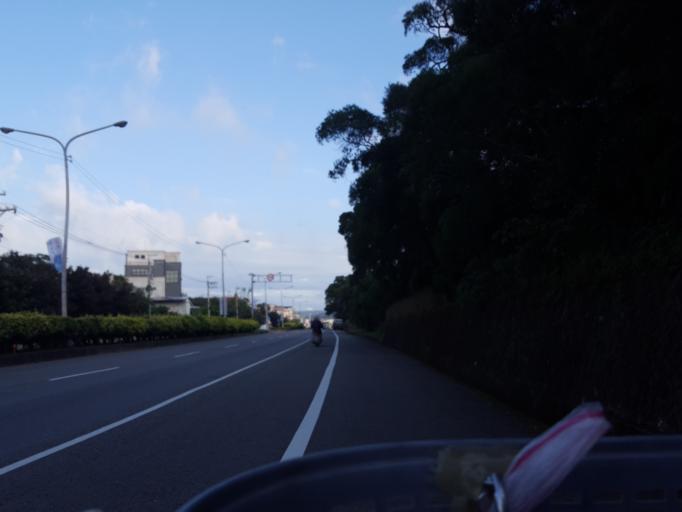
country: TW
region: Taiwan
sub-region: Hsinchu
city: Zhubei
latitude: 24.8850
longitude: 121.0236
